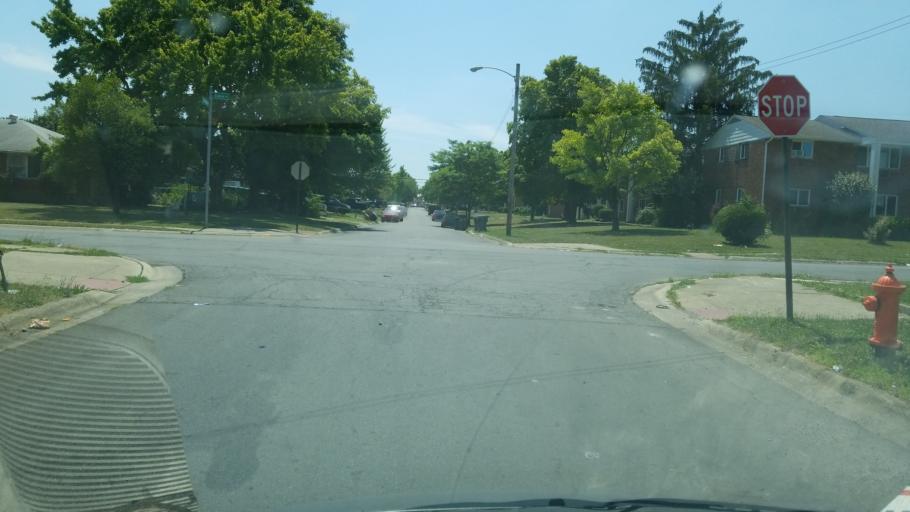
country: US
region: Ohio
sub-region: Franklin County
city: Lincoln Village
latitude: 39.9394
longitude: -83.0951
